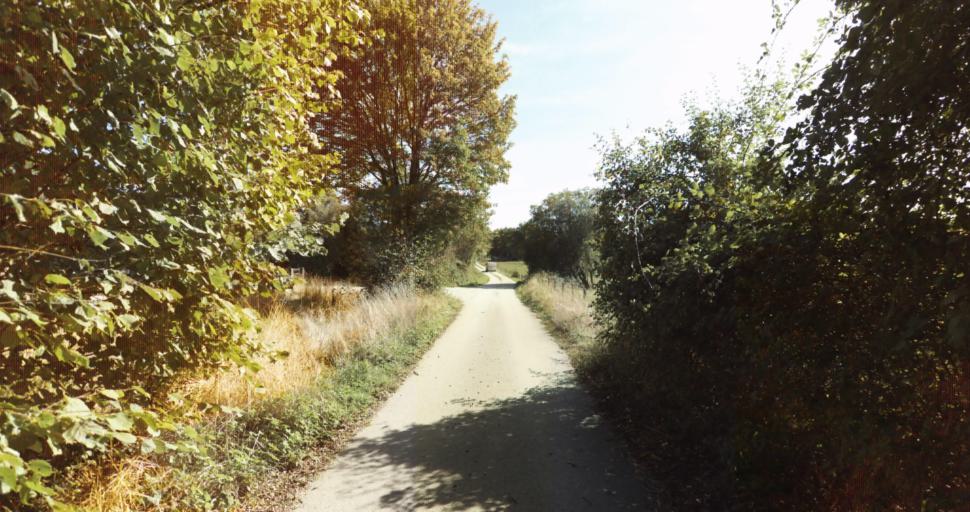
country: FR
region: Lower Normandy
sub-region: Departement de l'Orne
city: Gace
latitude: 48.7242
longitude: 0.2468
